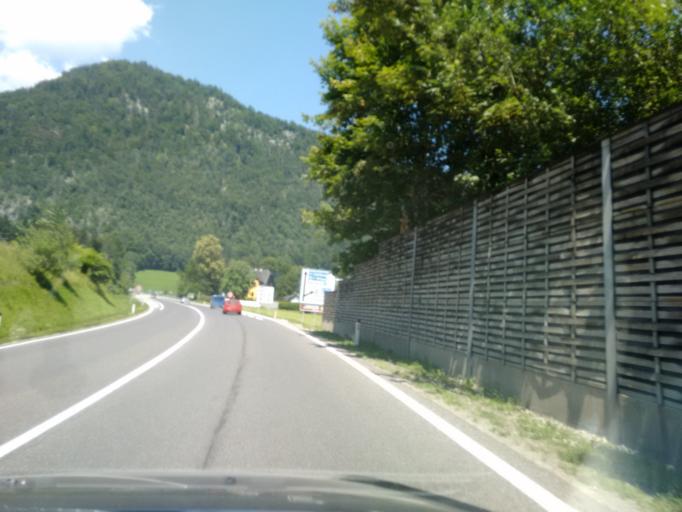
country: AT
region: Upper Austria
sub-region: Politischer Bezirk Gmunden
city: Bad Ischl
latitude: 47.7136
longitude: 13.6310
